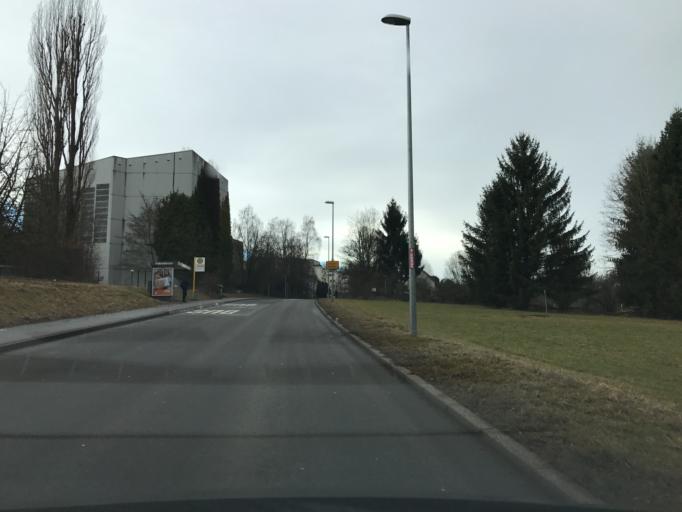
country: DE
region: Baden-Wuerttemberg
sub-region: Regierungsbezirk Stuttgart
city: Ostfildern
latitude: 48.7276
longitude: 9.2067
